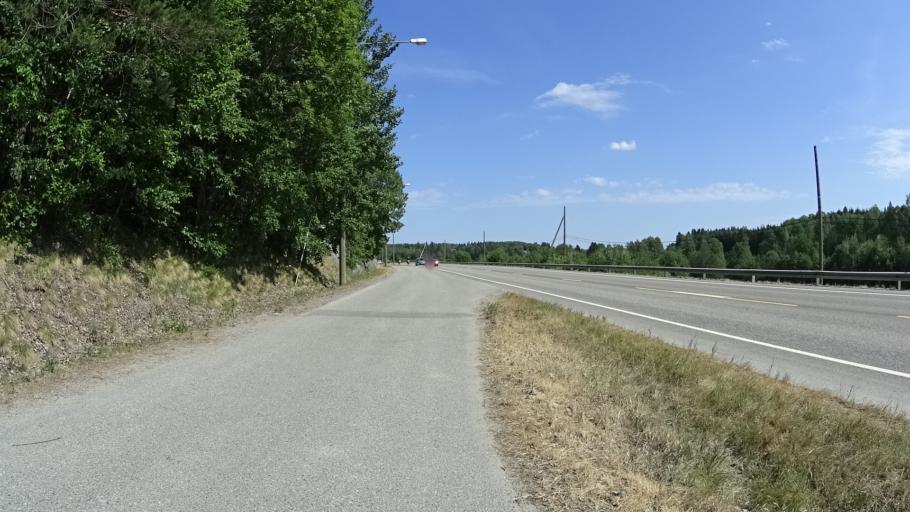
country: FI
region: Uusimaa
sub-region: Raaseporin
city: Karis
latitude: 60.0957
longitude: 23.6127
